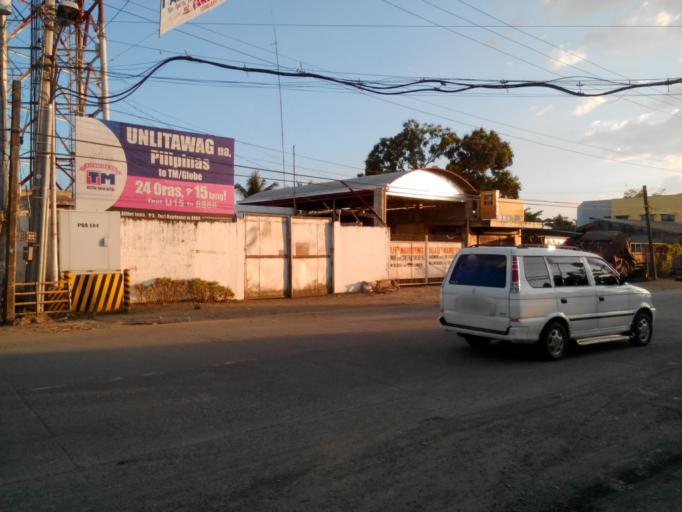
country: PH
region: Western Visayas
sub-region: Province of Iloilo
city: Passi
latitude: 11.1046
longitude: 122.6447
